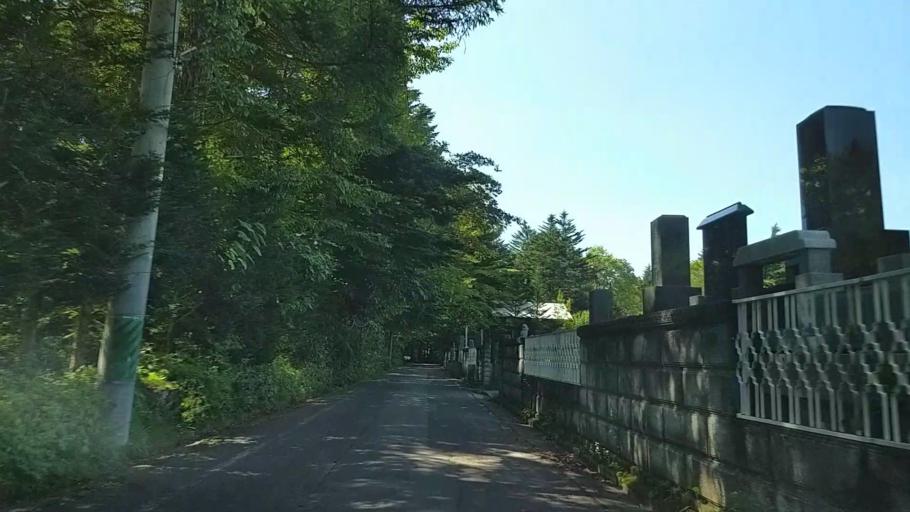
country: JP
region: Nagano
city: Saku
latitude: 36.3501
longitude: 138.6316
